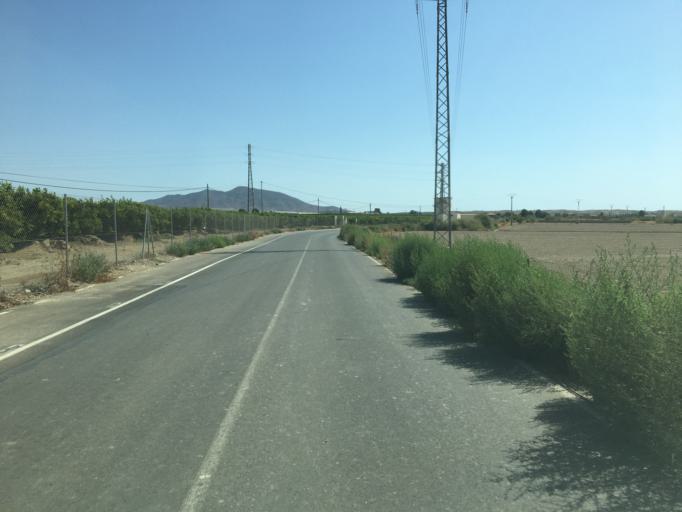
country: ES
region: Andalusia
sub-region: Provincia de Almeria
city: Huercal-Overa
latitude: 37.4209
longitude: -1.9052
